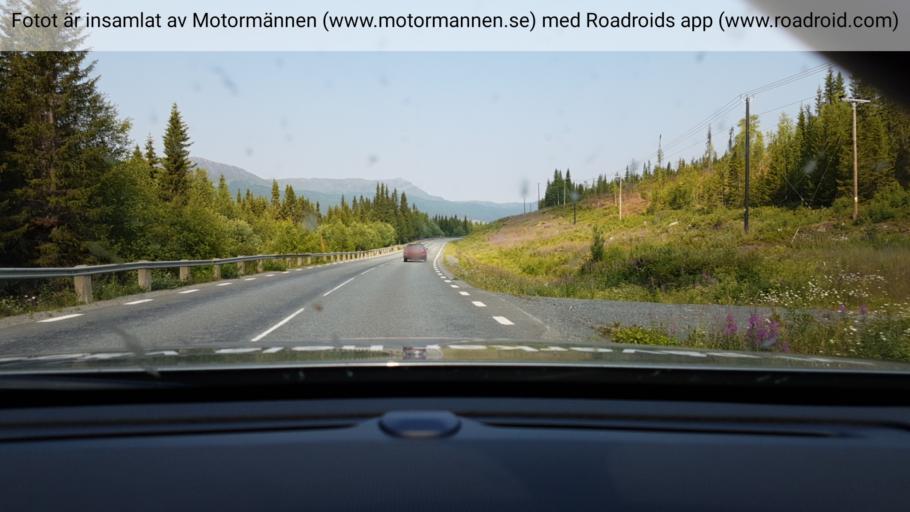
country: SE
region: Vaesterbotten
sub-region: Vilhelmina Kommun
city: Sjoberg
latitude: 65.5551
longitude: 15.5457
